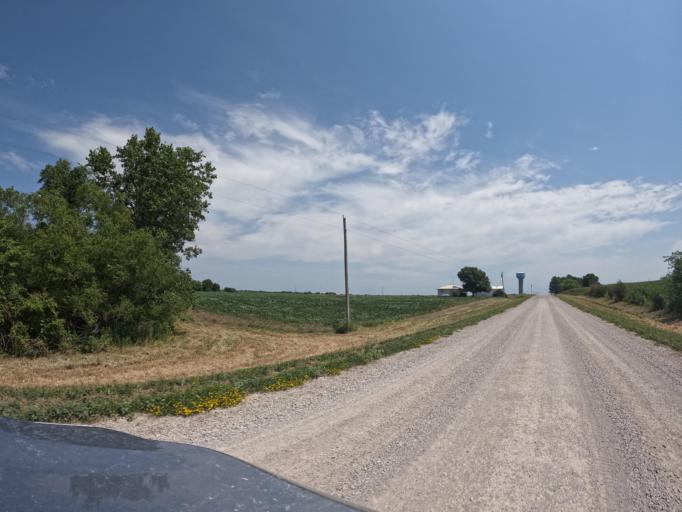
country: US
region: Iowa
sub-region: Appanoose County
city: Centerville
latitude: 40.7868
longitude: -92.9184
